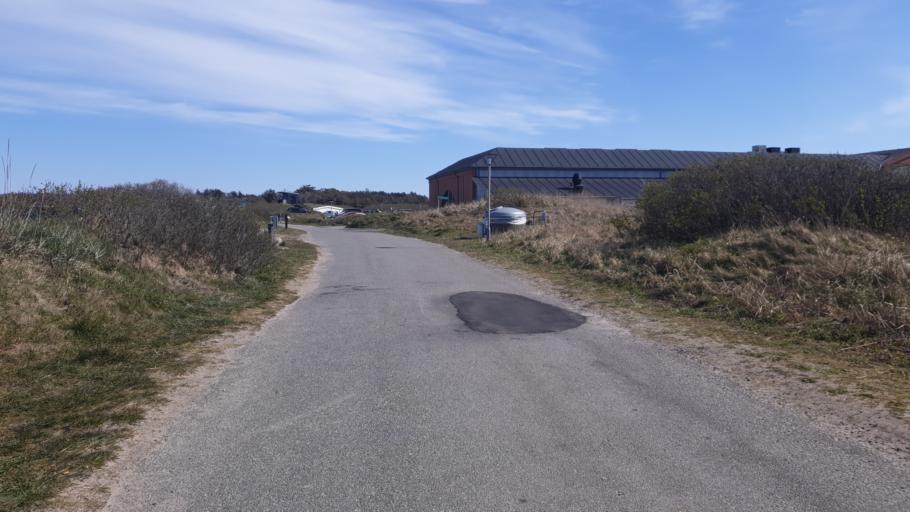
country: DK
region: North Denmark
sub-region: Hjorring Kommune
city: Hjorring
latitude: 57.4945
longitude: 9.8352
